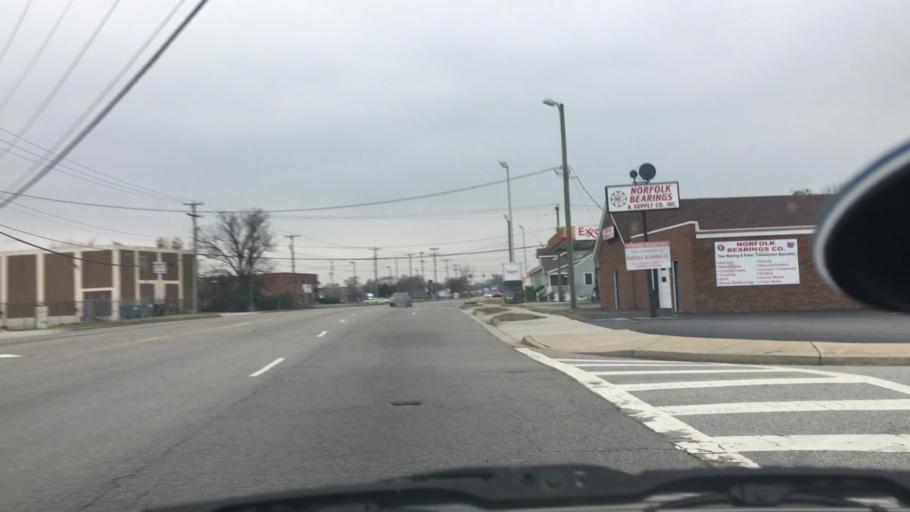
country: US
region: Virginia
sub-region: City of Norfolk
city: Norfolk
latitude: 36.8644
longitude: -76.2414
